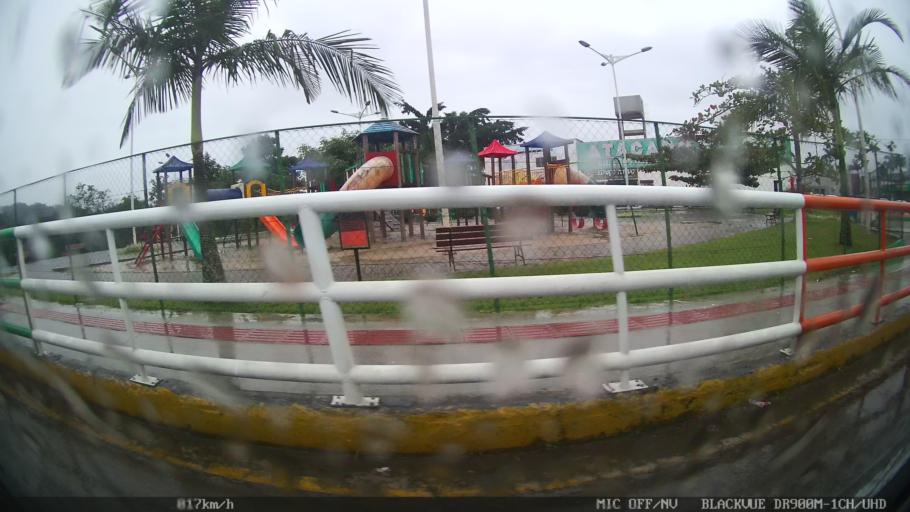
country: BR
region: Santa Catarina
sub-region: Balneario Camboriu
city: Balneario Camboriu
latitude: -27.0186
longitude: -48.6524
